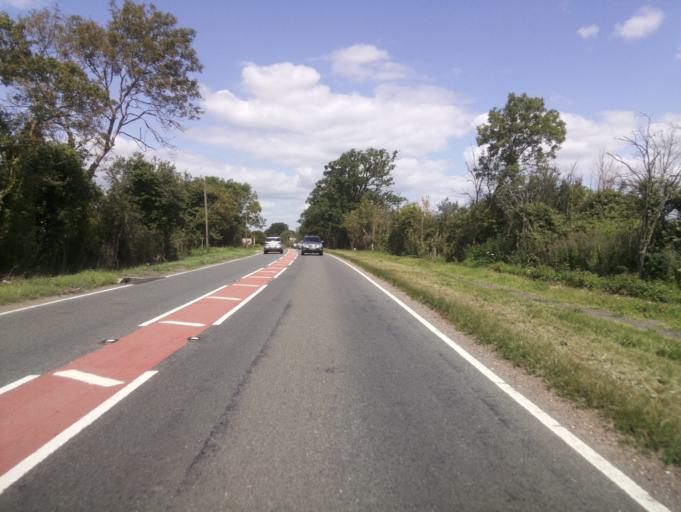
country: GB
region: England
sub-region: Buckinghamshire
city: Aylesbury
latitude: 51.8431
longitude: -0.8209
